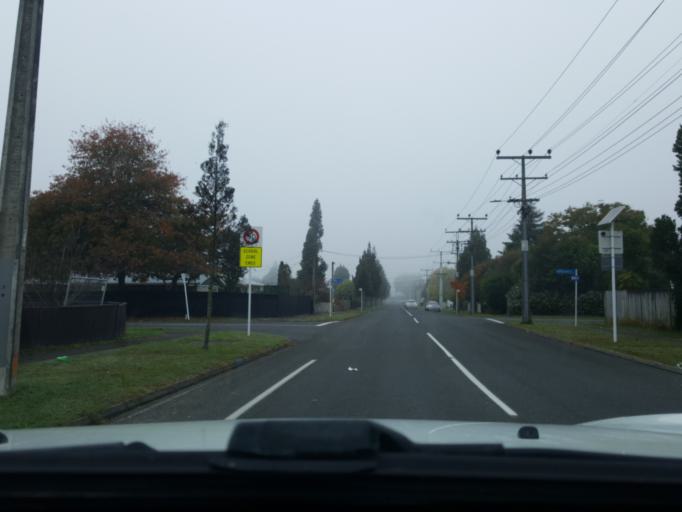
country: NZ
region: Waikato
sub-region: Hamilton City
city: Hamilton
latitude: -37.7685
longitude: 175.2331
